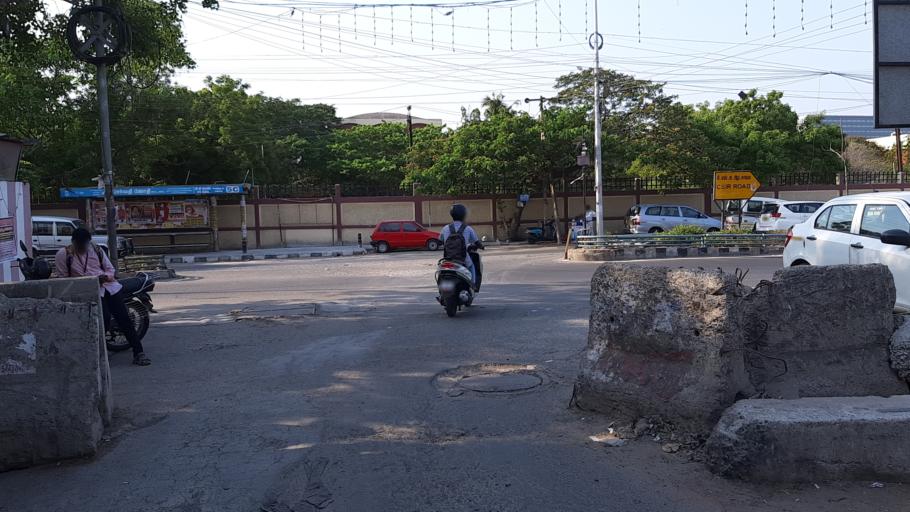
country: IN
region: Tamil Nadu
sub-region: Chennai
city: Gandhi Nagar
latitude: 12.9860
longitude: 80.2433
